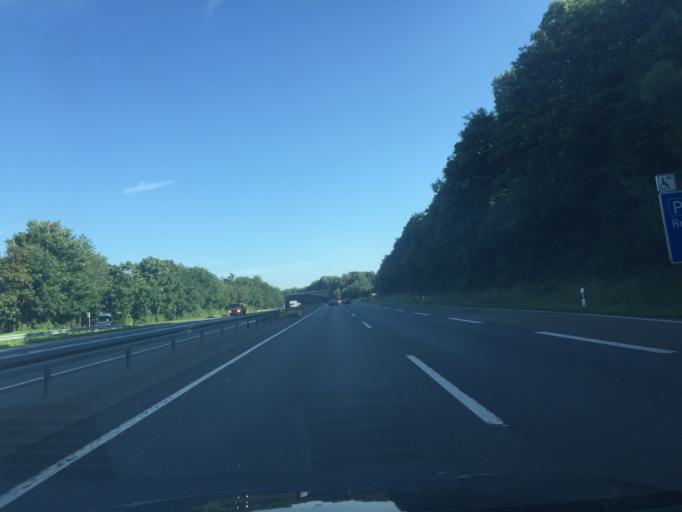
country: DE
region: North Rhine-Westphalia
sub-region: Regierungsbezirk Arnsberg
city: Nachrodt-Wiblingwerde
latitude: 51.2678
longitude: 7.6016
